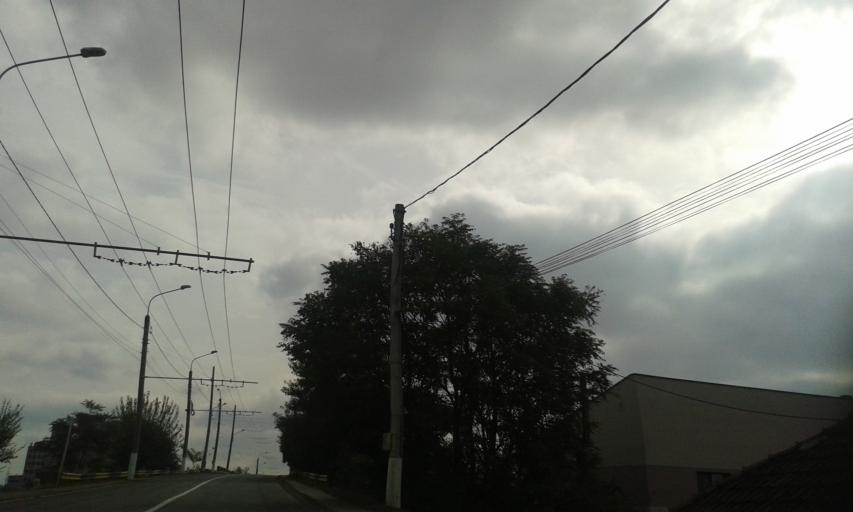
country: RO
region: Gorj
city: Targu Jiu
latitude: 45.0739
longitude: 23.3035
